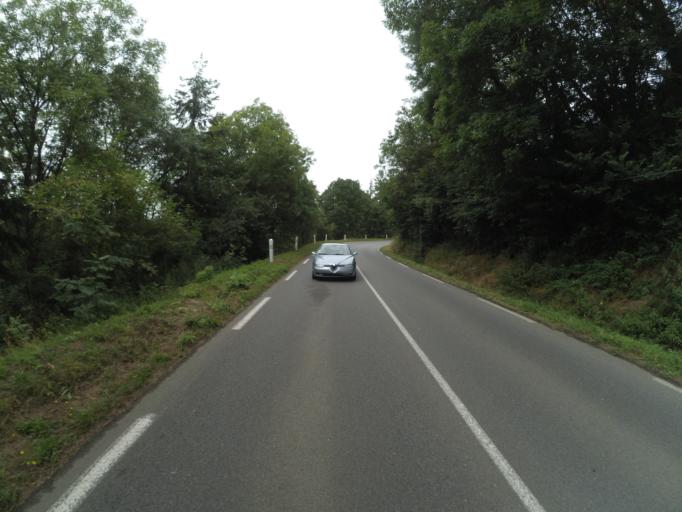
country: FR
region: Brittany
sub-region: Departement des Cotes-d'Armor
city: Tremuson
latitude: 48.5221
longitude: -2.8294
